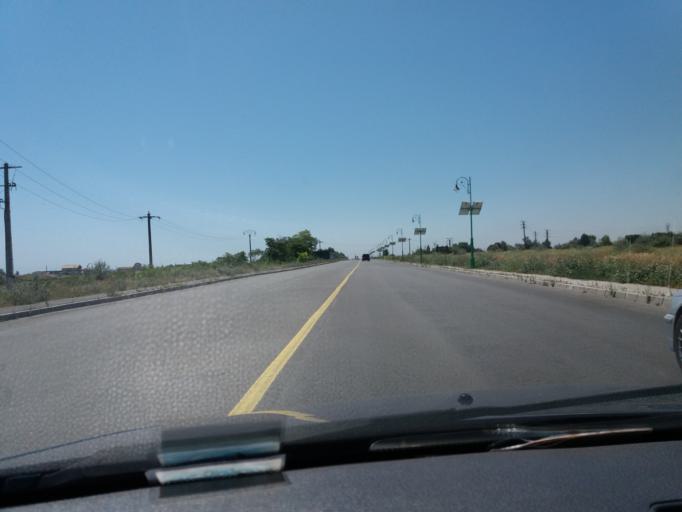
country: RO
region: Constanta
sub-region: Comuna Navodari
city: Navodari
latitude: 44.3024
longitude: 28.6145
